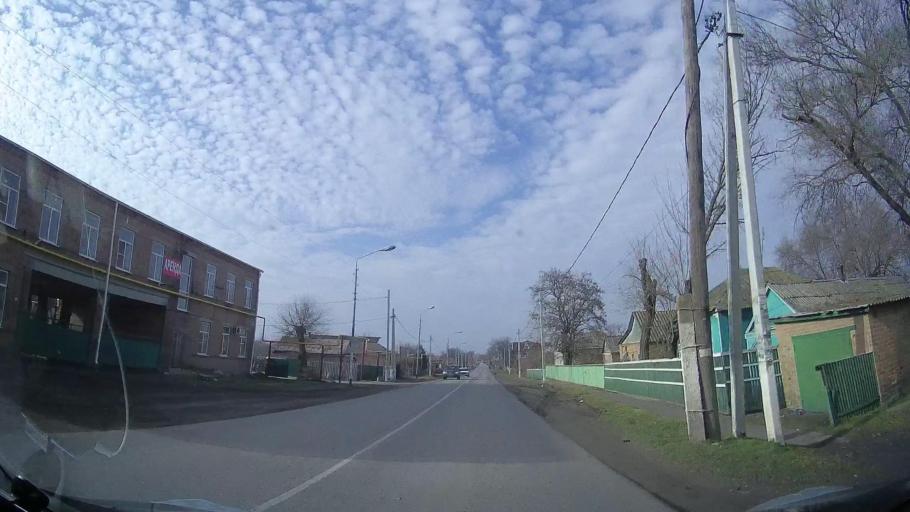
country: RU
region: Rostov
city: Veselyy
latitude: 47.0878
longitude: 40.7549
